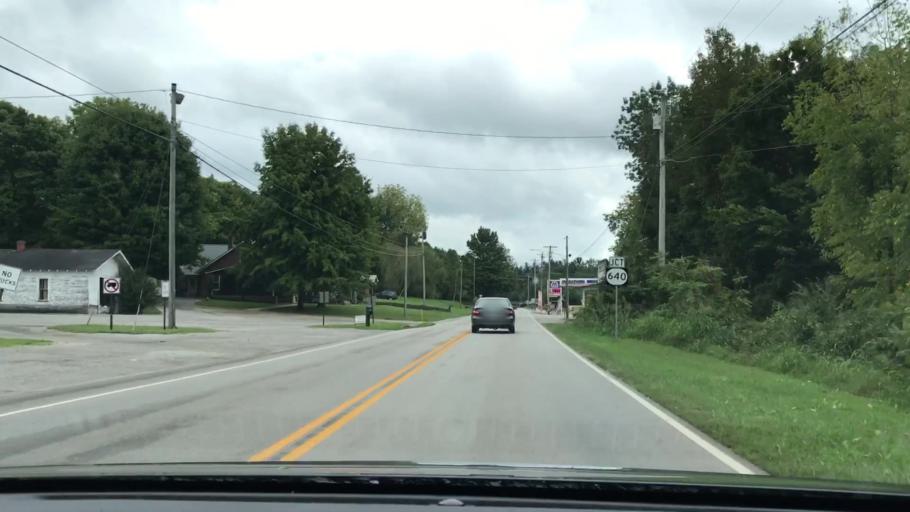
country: US
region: Kentucky
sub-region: Metcalfe County
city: Edmonton
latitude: 36.8860
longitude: -85.7077
